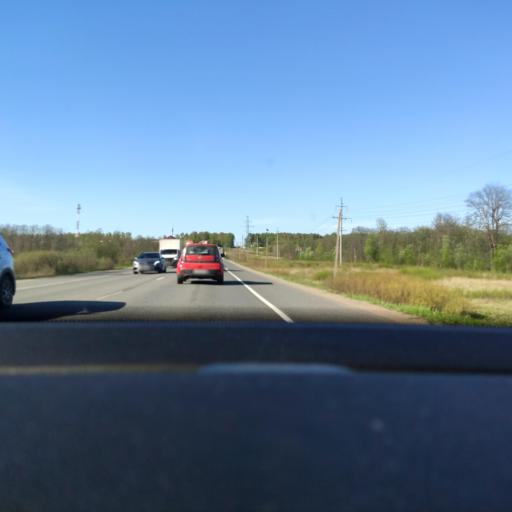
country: RU
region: Moskovskaya
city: Dmitrov
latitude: 56.3512
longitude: 37.4862
